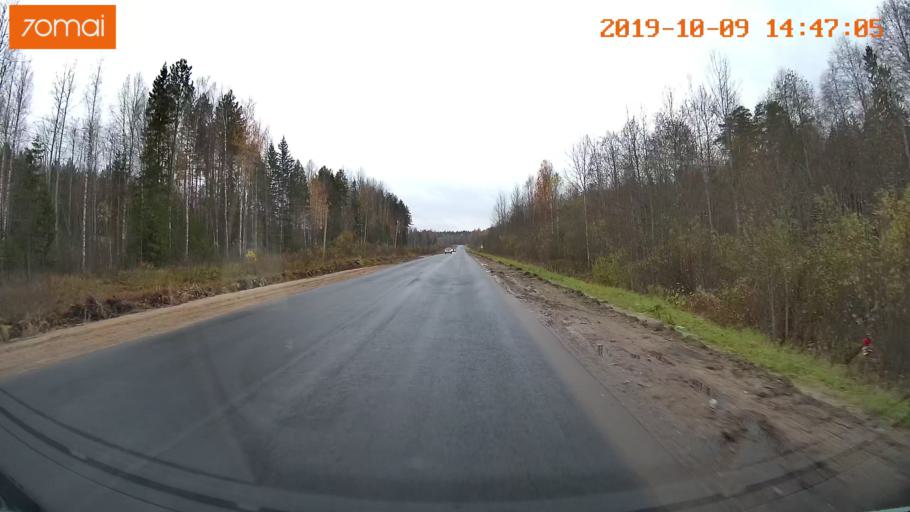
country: RU
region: Kostroma
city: Buy
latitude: 58.4225
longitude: 41.5741
